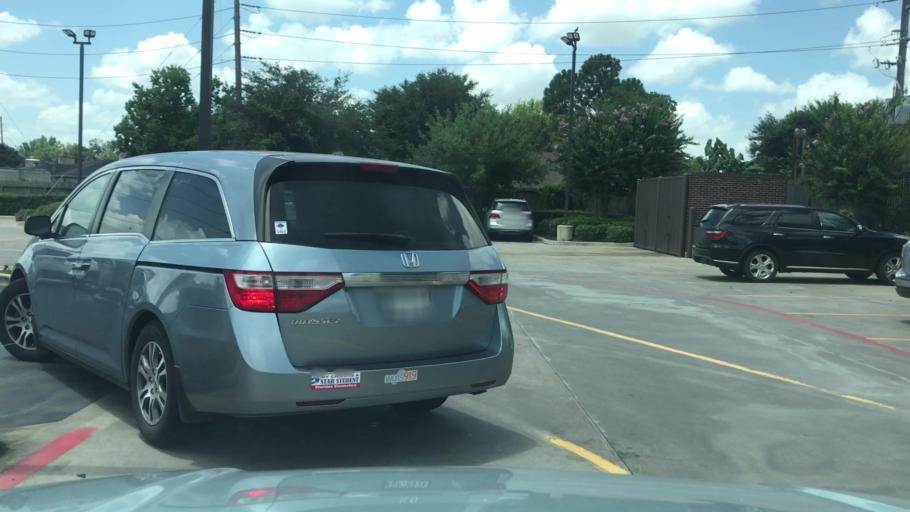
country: US
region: Texas
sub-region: Fort Bend County
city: Cinco Ranch
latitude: 29.7827
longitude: -95.7535
